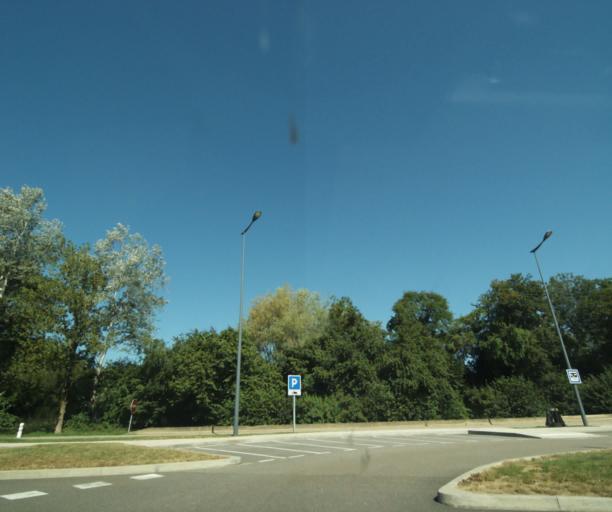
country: FR
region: Champagne-Ardenne
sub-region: Departement de la Haute-Marne
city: Avrecourt
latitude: 47.9750
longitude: 5.4984
